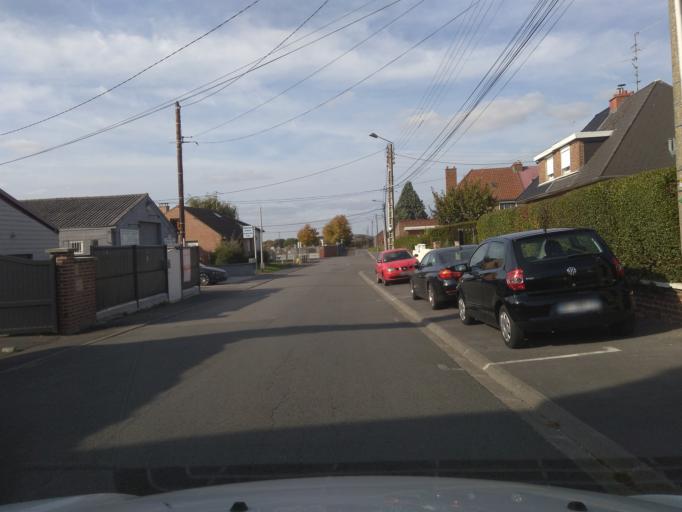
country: FR
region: Nord-Pas-de-Calais
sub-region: Departement du Nord
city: Saint-Saulve
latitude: 50.3747
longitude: 3.5635
